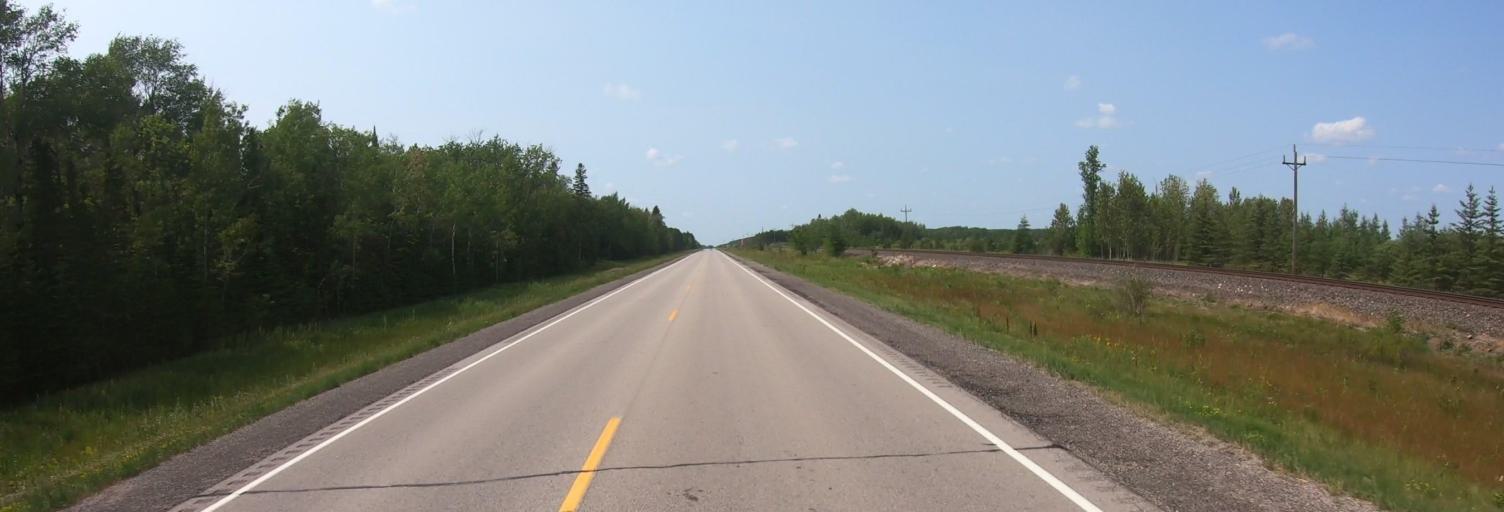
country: US
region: Minnesota
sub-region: Lake of the Woods County
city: Baudette
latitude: 48.7254
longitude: -94.7735
